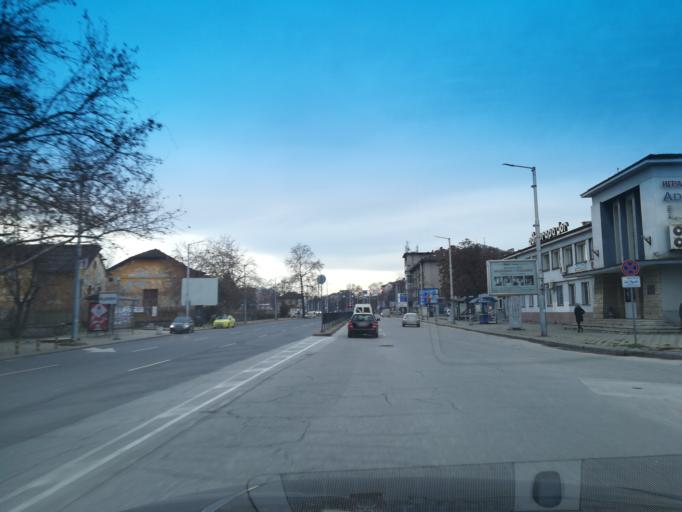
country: BG
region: Plovdiv
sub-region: Obshtina Plovdiv
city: Plovdiv
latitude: 42.1353
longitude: 24.7453
